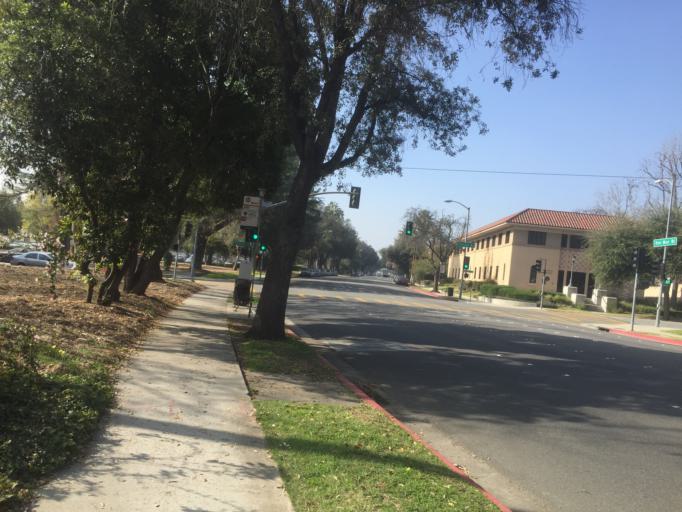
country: US
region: California
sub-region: Los Angeles County
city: Pasadena
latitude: 34.1410
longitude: -118.1240
